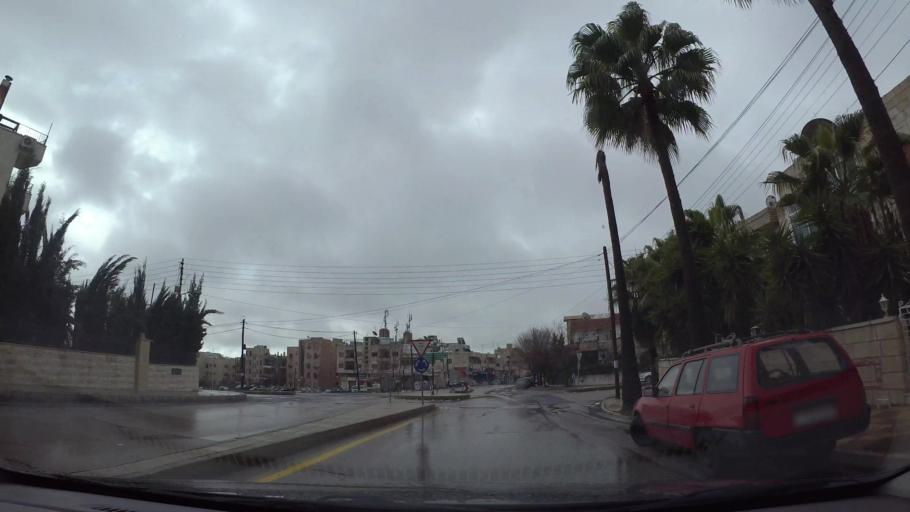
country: JO
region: Amman
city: Wadi as Sir
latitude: 31.9715
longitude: 35.8567
